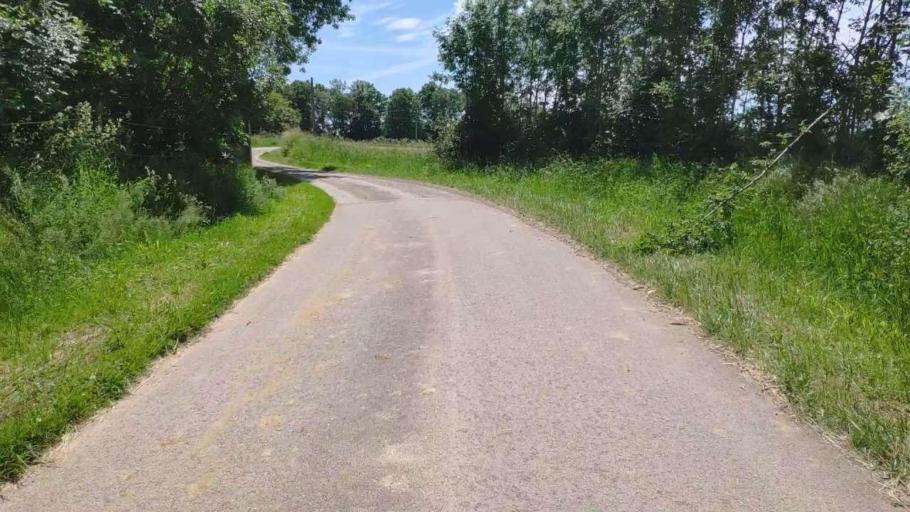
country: FR
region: Franche-Comte
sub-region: Departement du Jura
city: Bletterans
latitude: 46.7900
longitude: 5.3690
